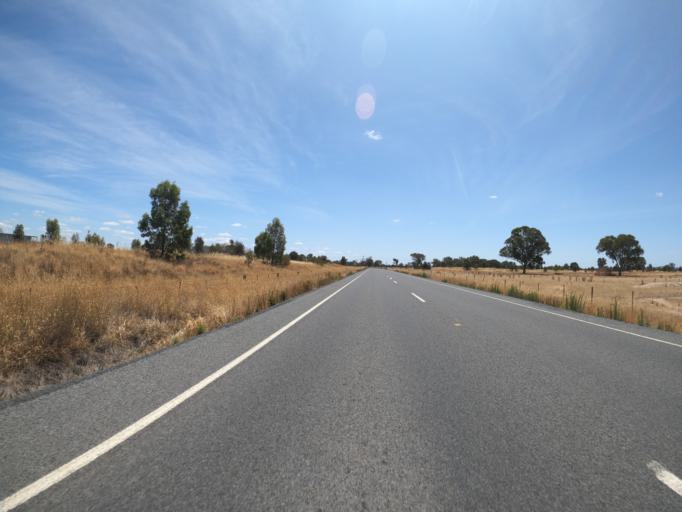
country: AU
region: Victoria
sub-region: Benalla
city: Benalla
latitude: -36.5194
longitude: 146.0341
